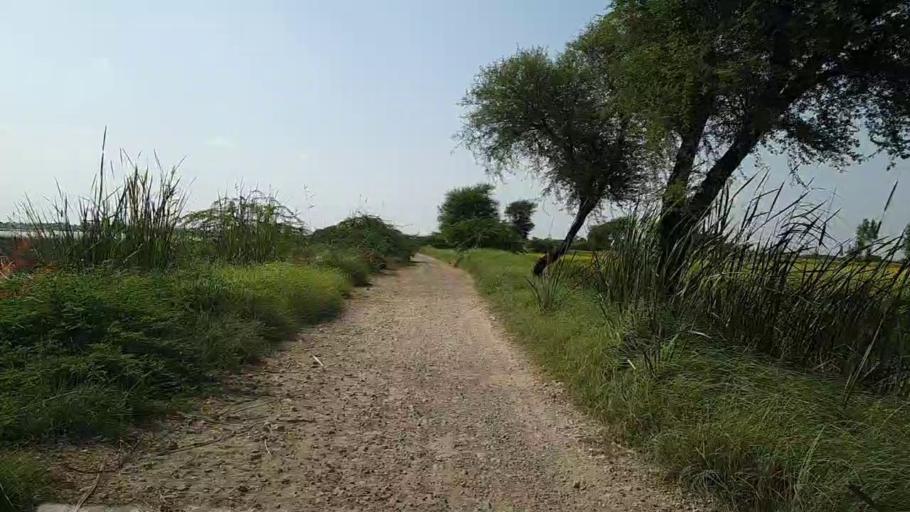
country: PK
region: Sindh
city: Kario
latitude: 24.7900
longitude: 68.5359
